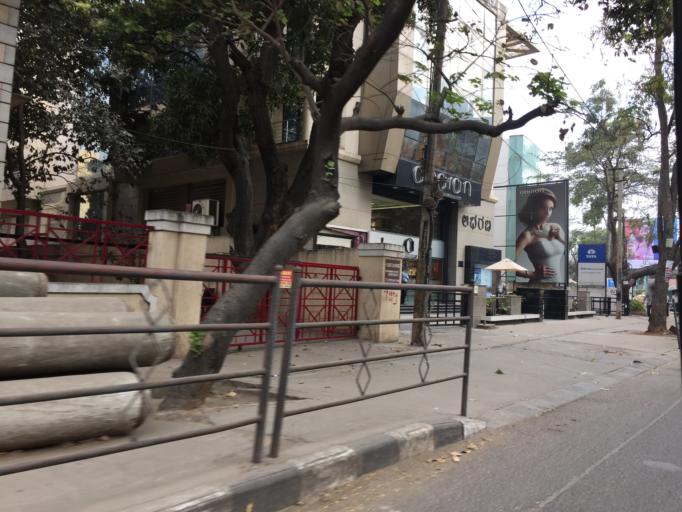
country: IN
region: Karnataka
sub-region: Bangalore Urban
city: Bangalore
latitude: 12.9711
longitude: 77.6104
